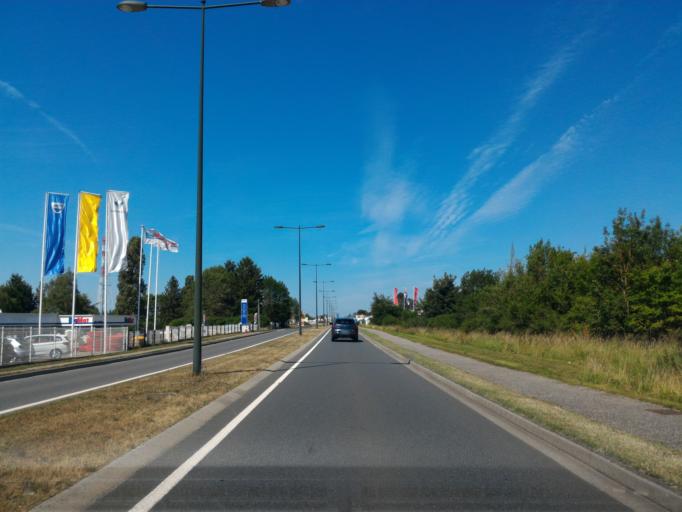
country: FR
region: Centre
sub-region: Departement de l'Indre
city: Saint-Maur
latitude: 46.7786
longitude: 1.6512
